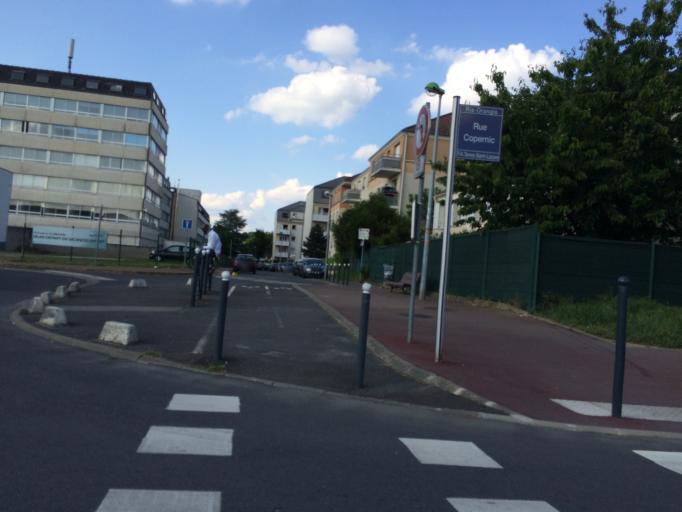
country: FR
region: Ile-de-France
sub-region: Departement de l'Essonne
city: Grigny
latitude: 48.6505
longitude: 2.3991
